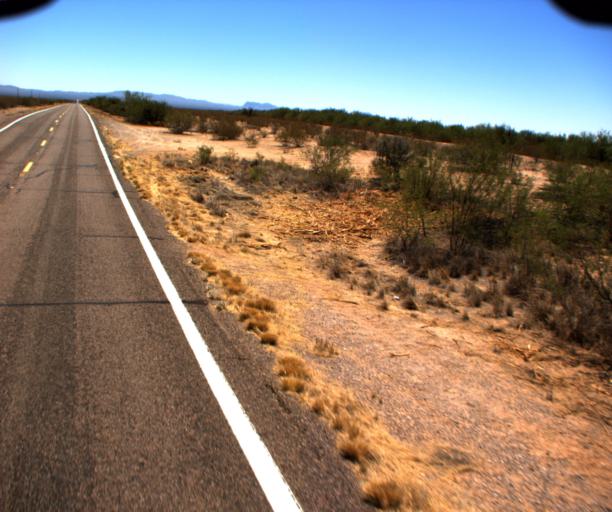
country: US
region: Arizona
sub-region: Pima County
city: Ajo
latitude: 32.2002
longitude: -112.4946
